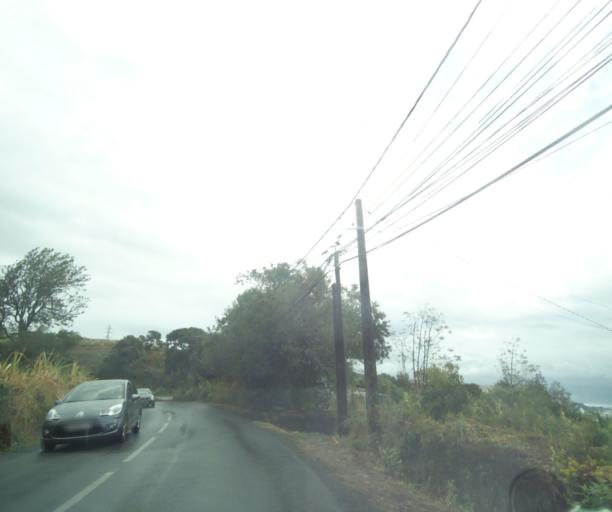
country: RE
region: Reunion
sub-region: Reunion
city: Saint-Paul
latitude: -21.0133
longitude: 55.3095
